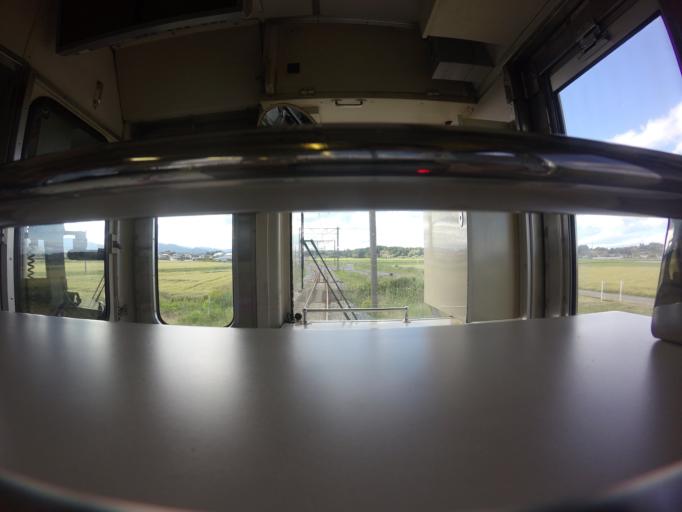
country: JP
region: Fukushima
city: Namie
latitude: 37.6026
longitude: 140.9944
